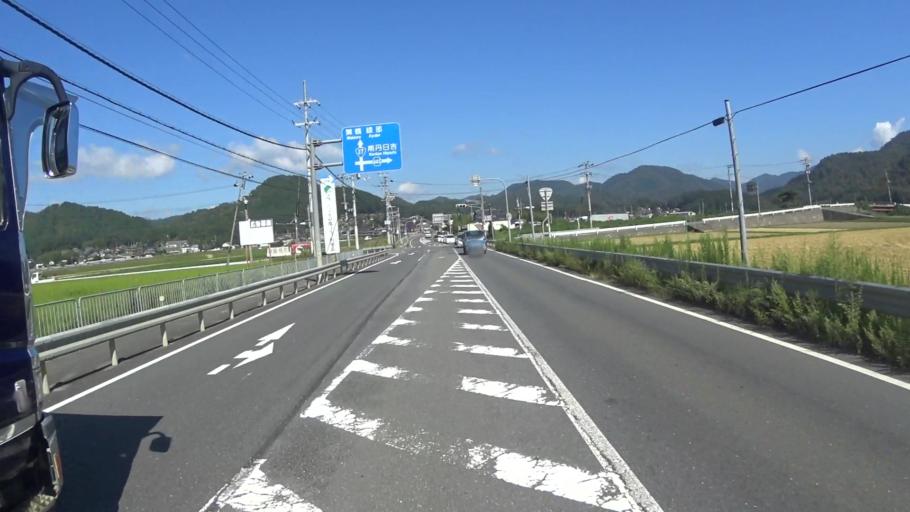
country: JP
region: Kyoto
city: Ayabe
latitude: 35.1819
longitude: 135.4197
